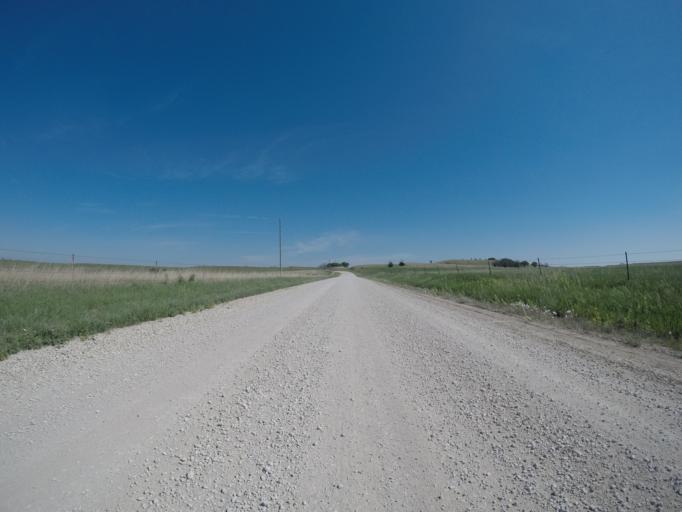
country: US
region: Kansas
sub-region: Wabaunsee County
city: Alma
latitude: 39.0126
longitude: -96.1137
